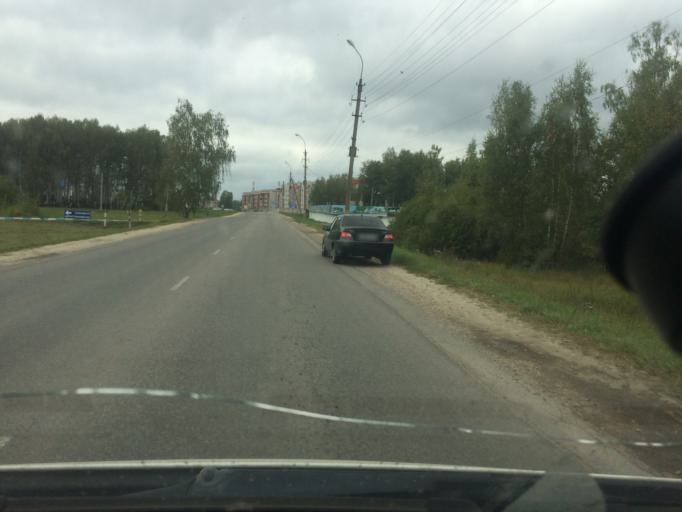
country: RU
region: Tula
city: Suvorov
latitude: 54.1150
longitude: 36.5133
